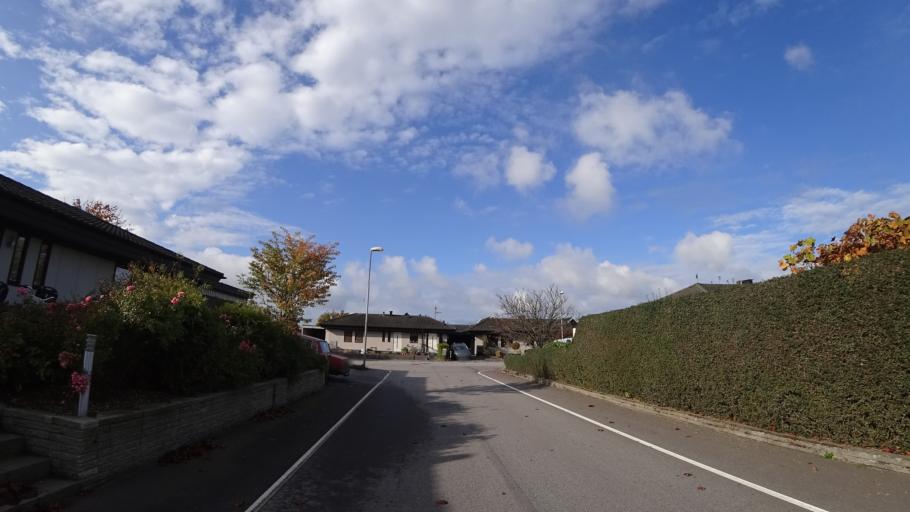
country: SE
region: Skane
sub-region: Staffanstorps Kommun
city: Staffanstorp
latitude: 55.6345
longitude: 13.1889
